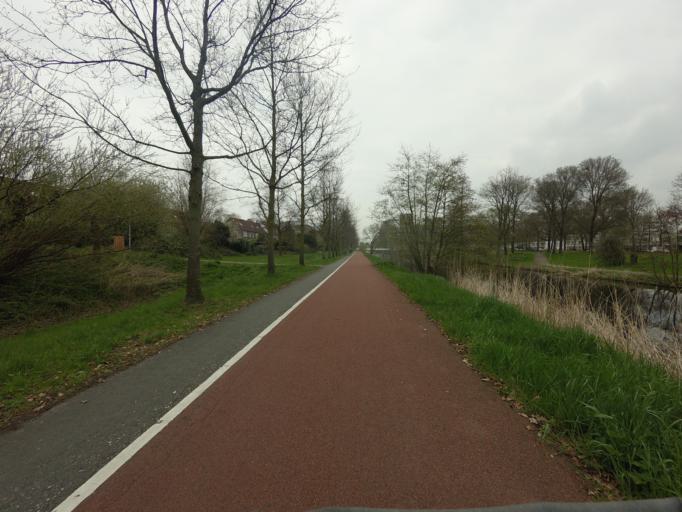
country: NL
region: Utrecht
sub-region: Gemeente Utrecht
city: Utrecht
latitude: 52.1218
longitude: 5.0940
